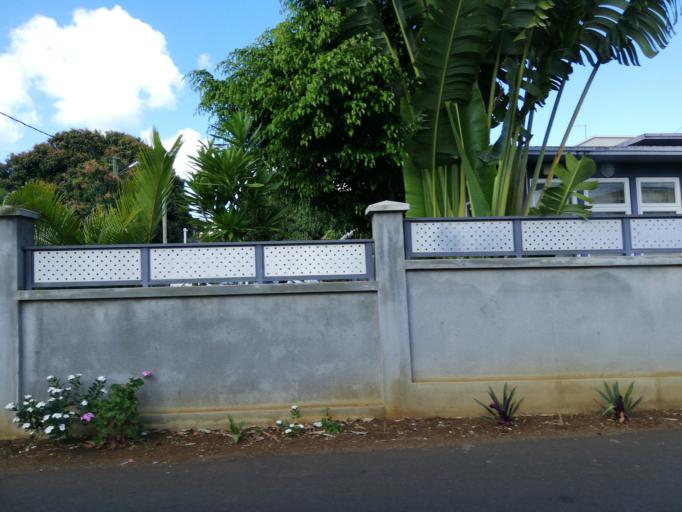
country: MU
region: Moka
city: Moka
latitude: -20.2279
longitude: 57.4718
